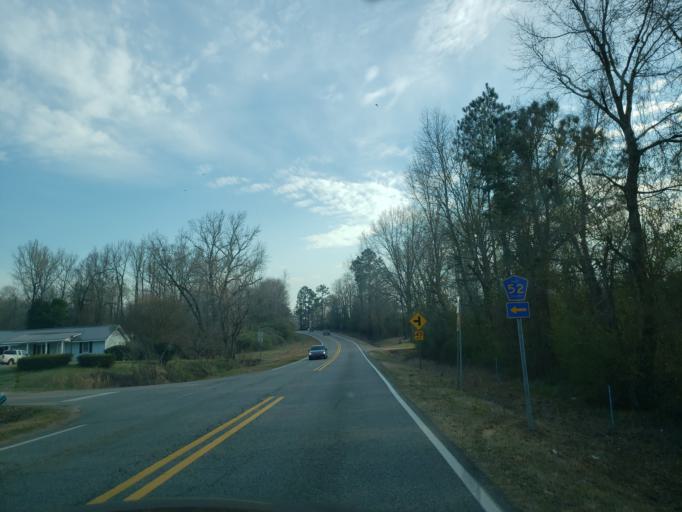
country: US
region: Alabama
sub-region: Hale County
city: Moundville
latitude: 32.9691
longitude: -87.6250
